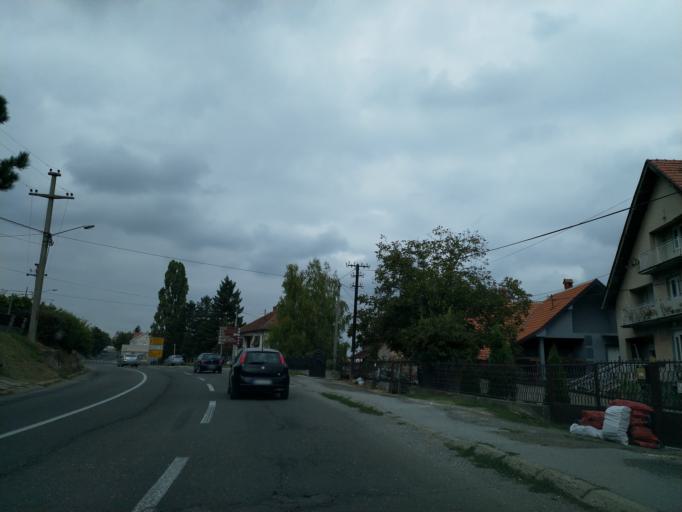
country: RS
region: Central Serbia
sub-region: Sumadijski Okrug
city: Topola
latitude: 44.2493
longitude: 20.6896
